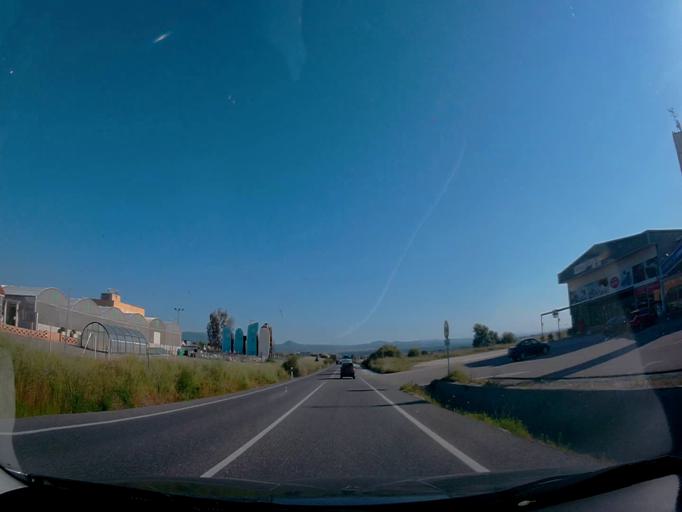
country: ES
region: Castille-La Mancha
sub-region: Province of Toledo
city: Escalona
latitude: 40.1330
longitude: -4.4047
